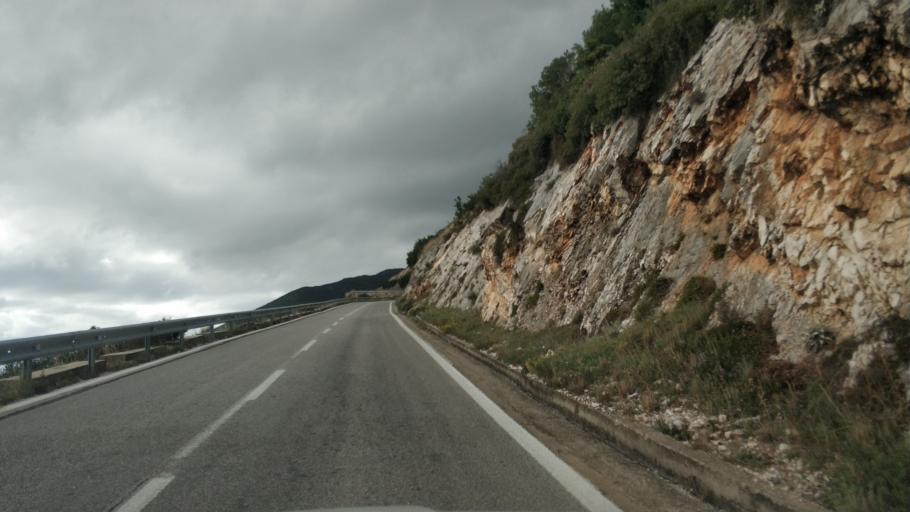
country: AL
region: Vlore
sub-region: Rrethi i Vlores
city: Vranisht
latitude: 40.1789
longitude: 19.5959
